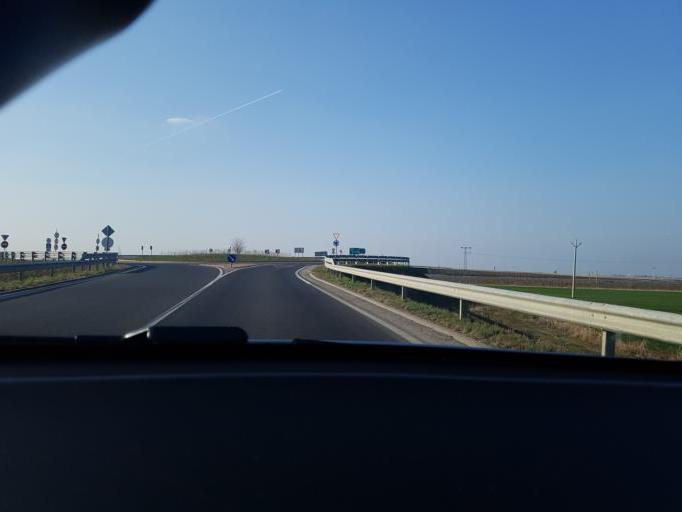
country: HU
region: Csongrad
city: Csanadpalota
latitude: 46.2139
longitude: 20.7156
